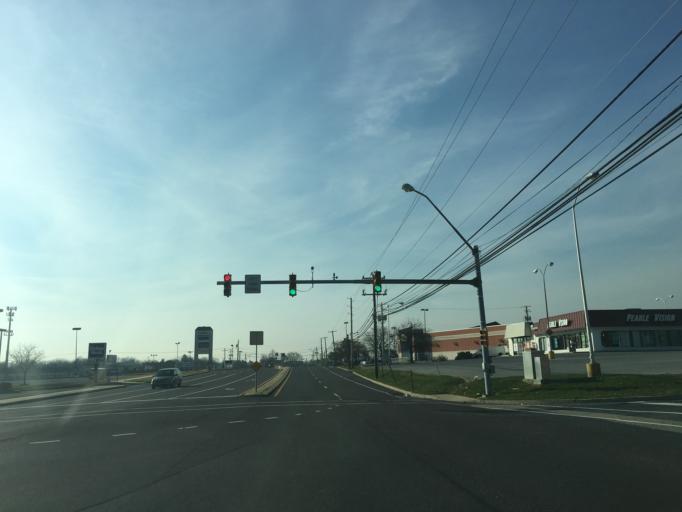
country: US
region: Pennsylvania
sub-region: Dauphin County
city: Colonial Park
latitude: 40.3089
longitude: -76.8036
